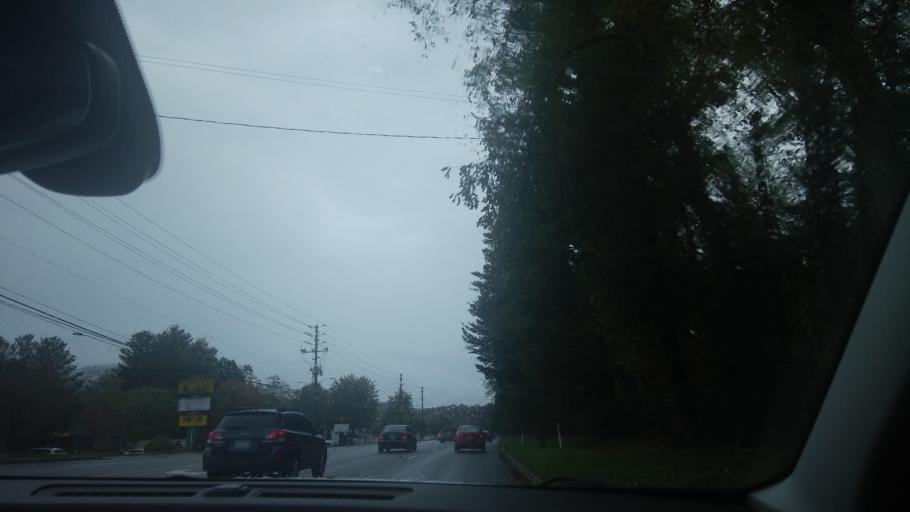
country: US
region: North Carolina
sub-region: Buncombe County
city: Biltmore Forest
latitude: 35.5479
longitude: -82.5349
